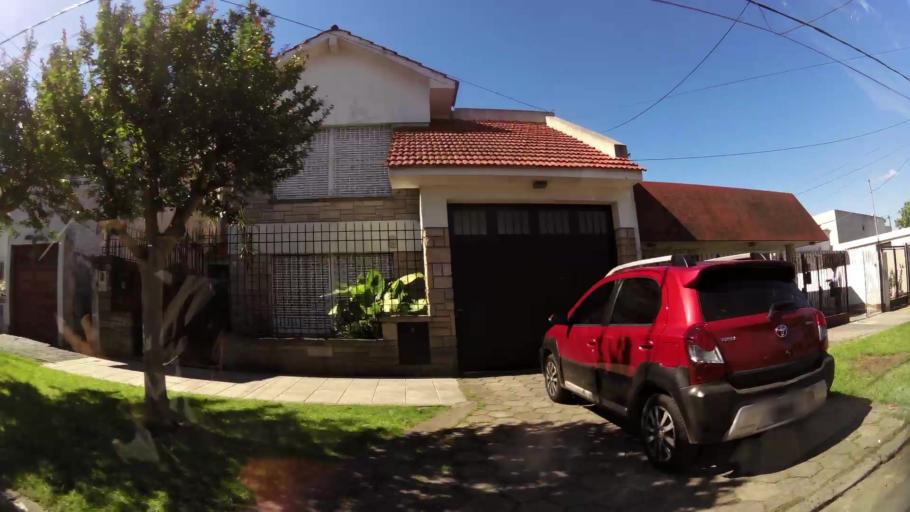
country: AR
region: Buenos Aires
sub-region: Partido de Lomas de Zamora
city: Lomas de Zamora
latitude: -34.7562
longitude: -58.4143
